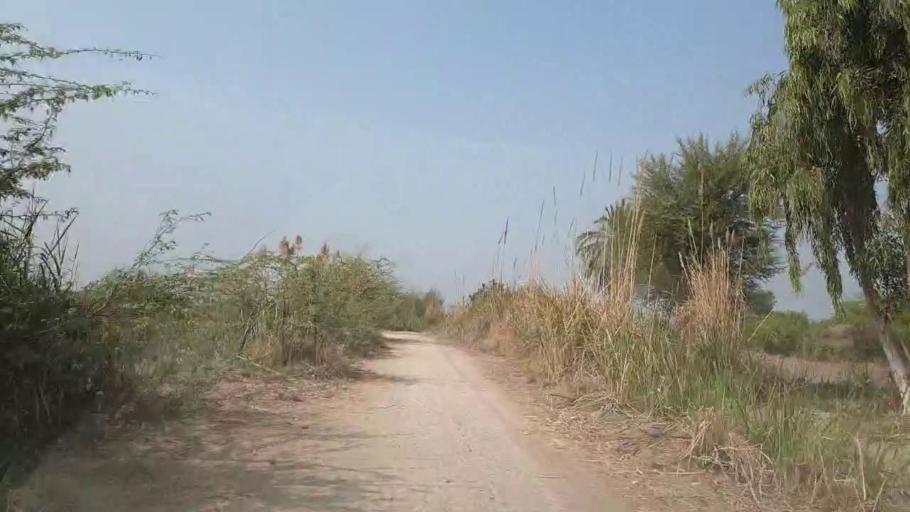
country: PK
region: Sindh
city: Mirpur Khas
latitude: 25.5715
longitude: 69.1394
